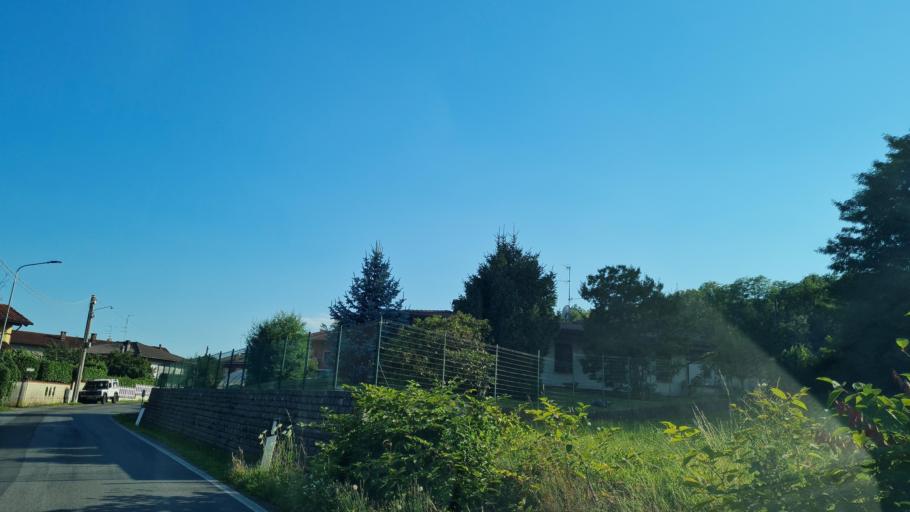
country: IT
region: Piedmont
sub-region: Provincia di Biella
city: Camburzano
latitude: 45.5526
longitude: 8.0079
